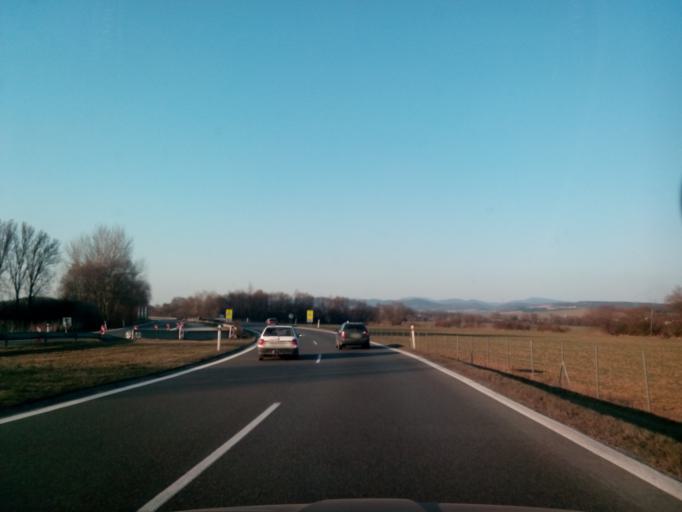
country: SK
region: Kosicky
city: Kosice
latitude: 48.7899
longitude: 21.3129
